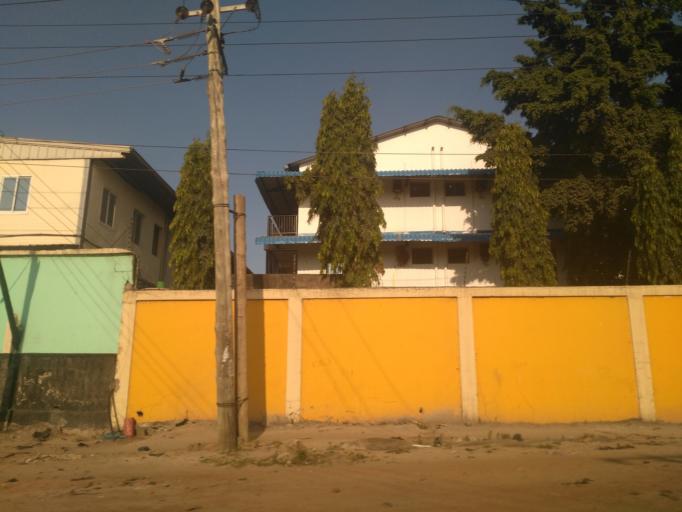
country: TZ
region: Dar es Salaam
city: Dar es Salaam
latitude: -6.9139
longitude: 39.2655
